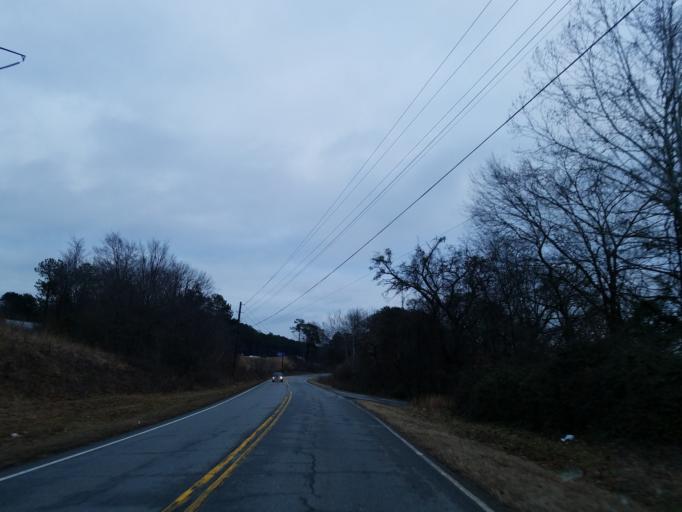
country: US
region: Georgia
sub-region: Cobb County
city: Acworth
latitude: 34.0873
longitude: -84.7101
